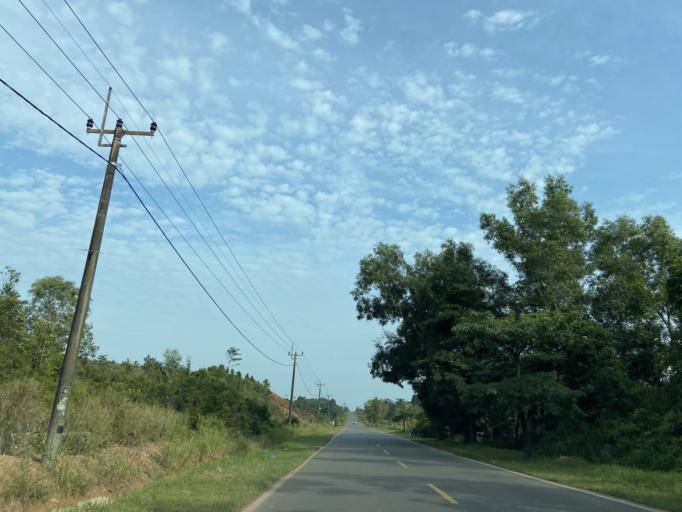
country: ID
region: Riau Islands
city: Tanjungpinang
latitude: 0.9012
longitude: 104.1302
